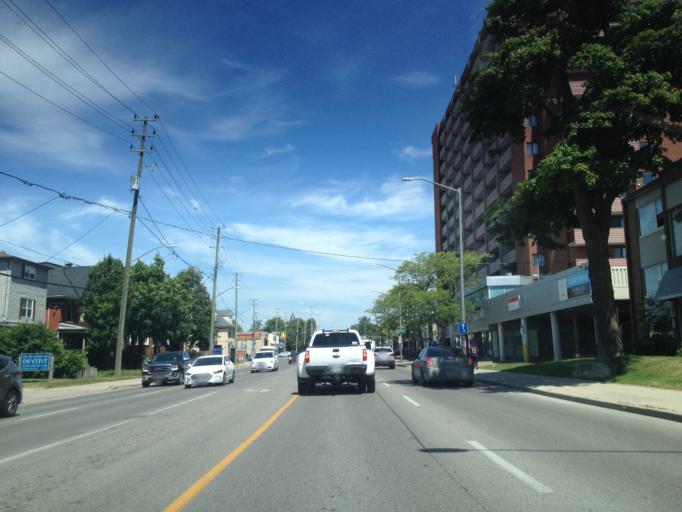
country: CA
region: Ontario
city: London
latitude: 42.9948
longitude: -81.2554
